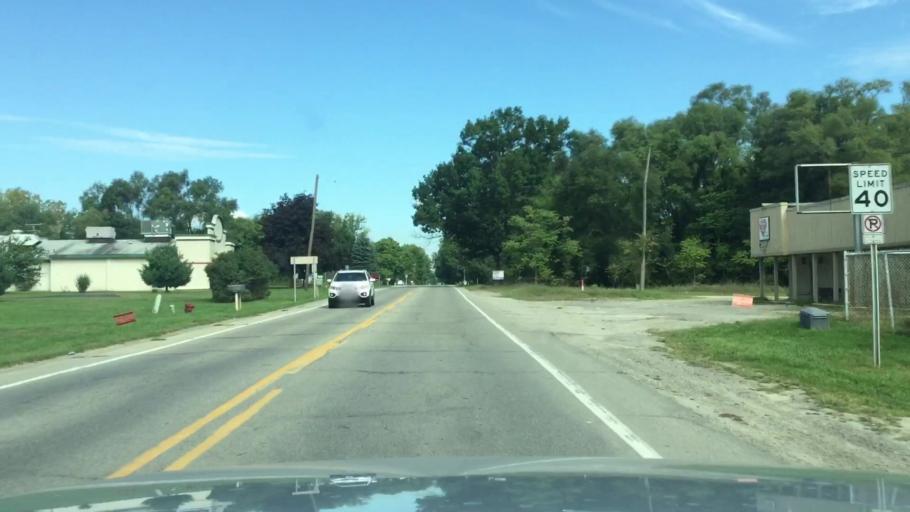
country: US
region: Michigan
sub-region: Wayne County
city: Belleville
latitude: 42.1615
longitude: -83.4824
